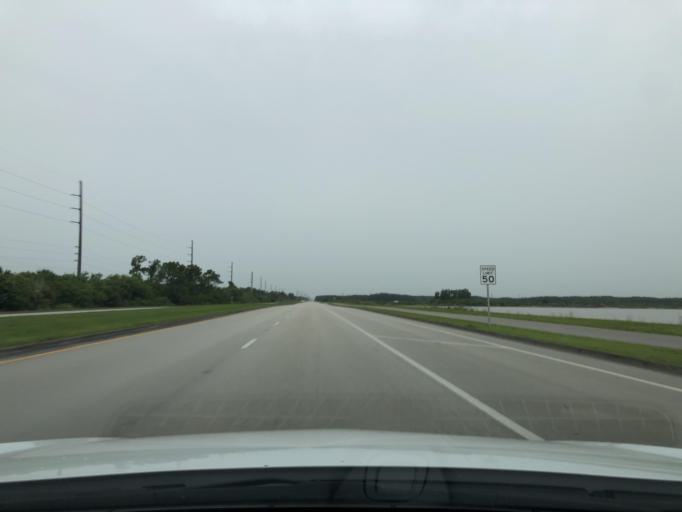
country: US
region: Florida
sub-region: Collier County
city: Immokalee
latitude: 26.2945
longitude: -81.4507
